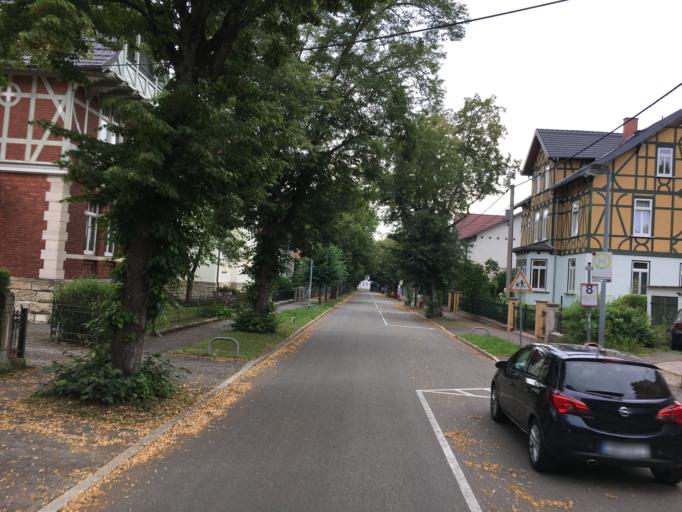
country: DE
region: Thuringia
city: Schmalkalden
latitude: 50.7282
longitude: 10.4541
